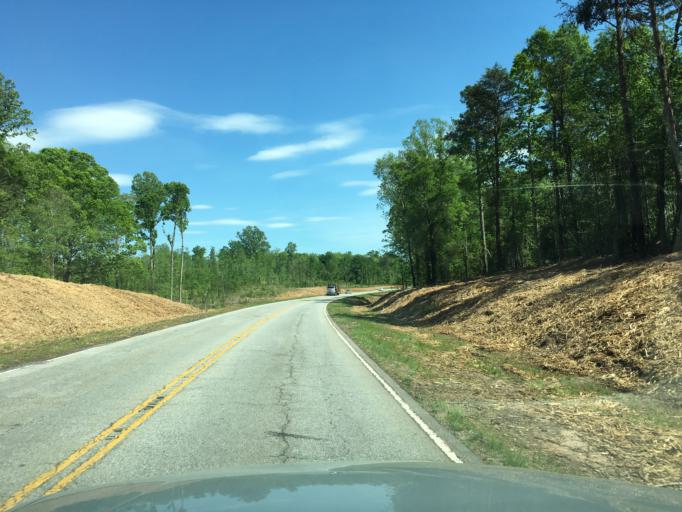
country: US
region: South Carolina
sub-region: Spartanburg County
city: Wellford
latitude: 34.9685
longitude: -82.0902
